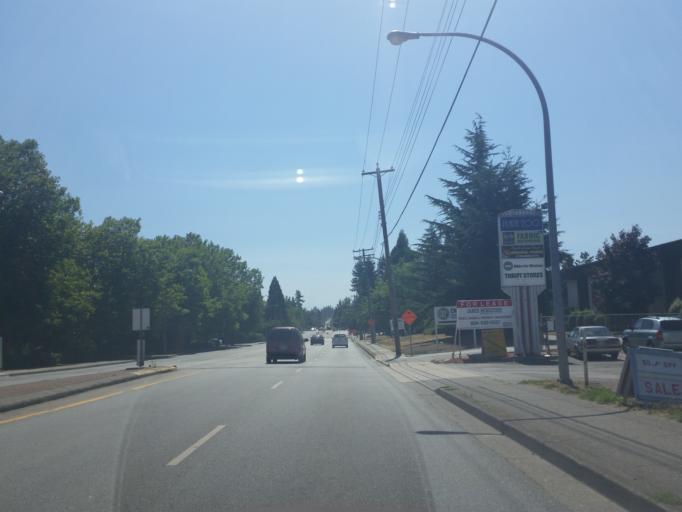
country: CA
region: British Columbia
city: Langley
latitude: 49.1109
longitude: -122.6689
